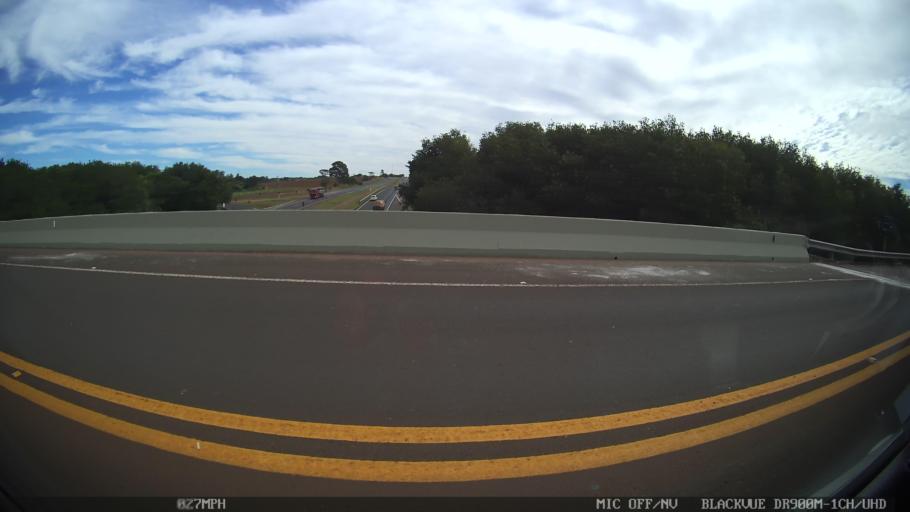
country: BR
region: Sao Paulo
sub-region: Santa Adelia
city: Santa Adelia
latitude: -21.3707
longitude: -48.7488
